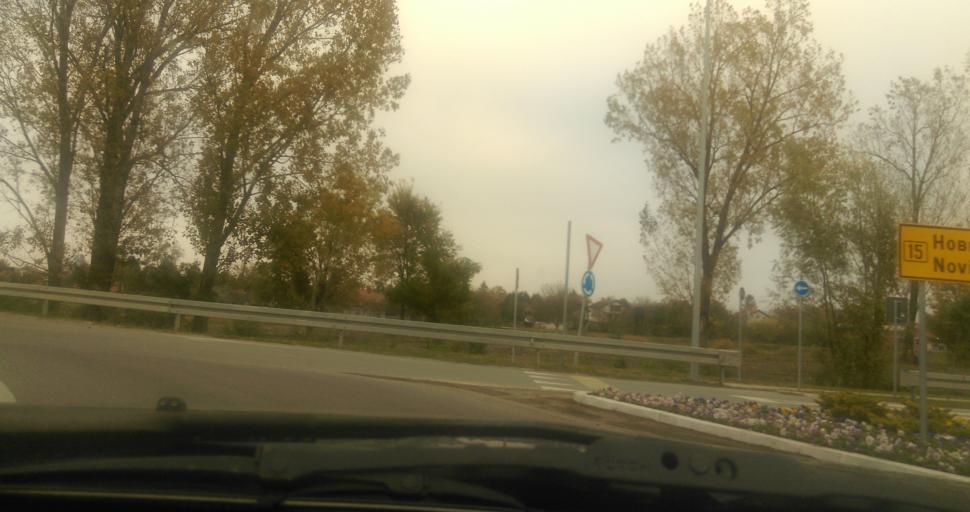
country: RS
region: Autonomna Pokrajina Vojvodina
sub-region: Juznobacki Okrug
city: Becej
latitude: 45.6006
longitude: 20.0393
